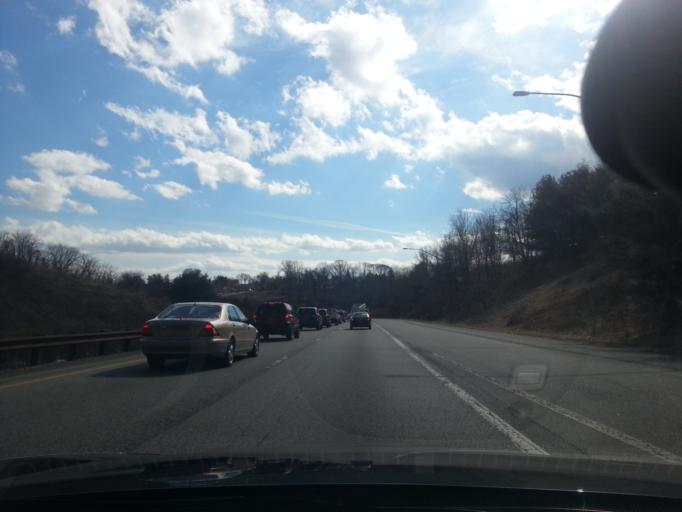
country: US
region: Pennsylvania
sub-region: Delaware County
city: Broomall
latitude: 39.9782
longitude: -75.3406
